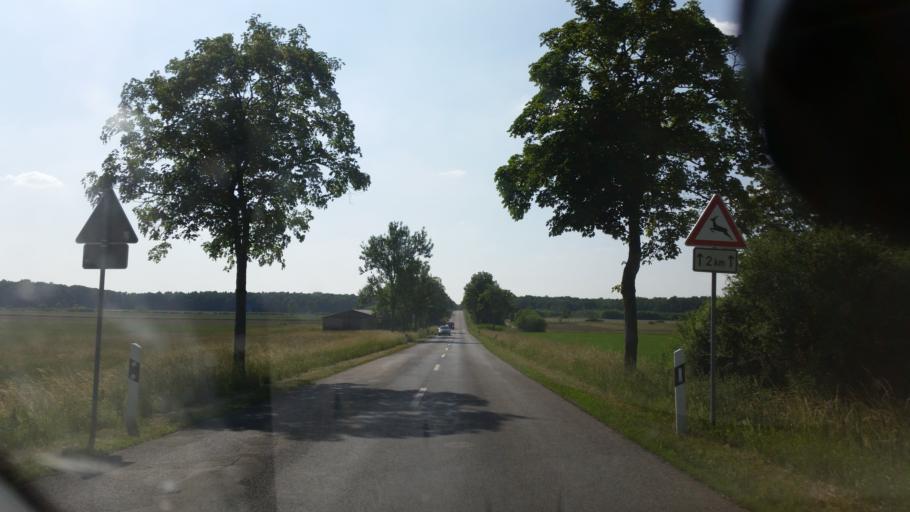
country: DE
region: Lower Saxony
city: Lehre
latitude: 52.3151
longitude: 10.7389
